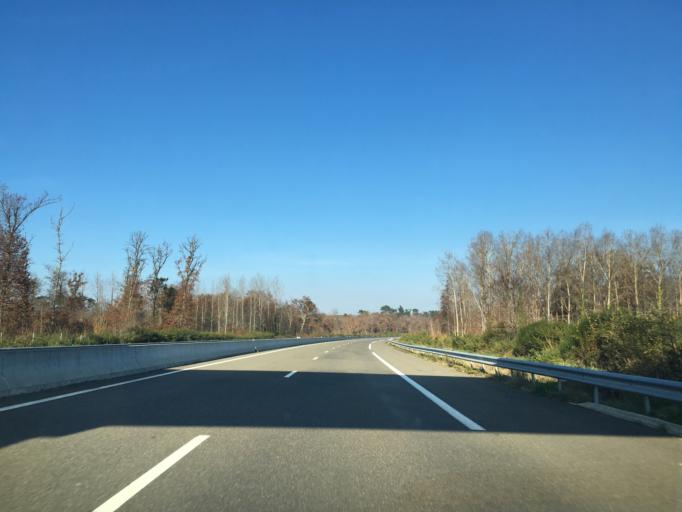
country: FR
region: Aquitaine
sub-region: Departement des Landes
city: Villeneuve-de-Marsan
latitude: 43.8677
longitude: -0.3596
